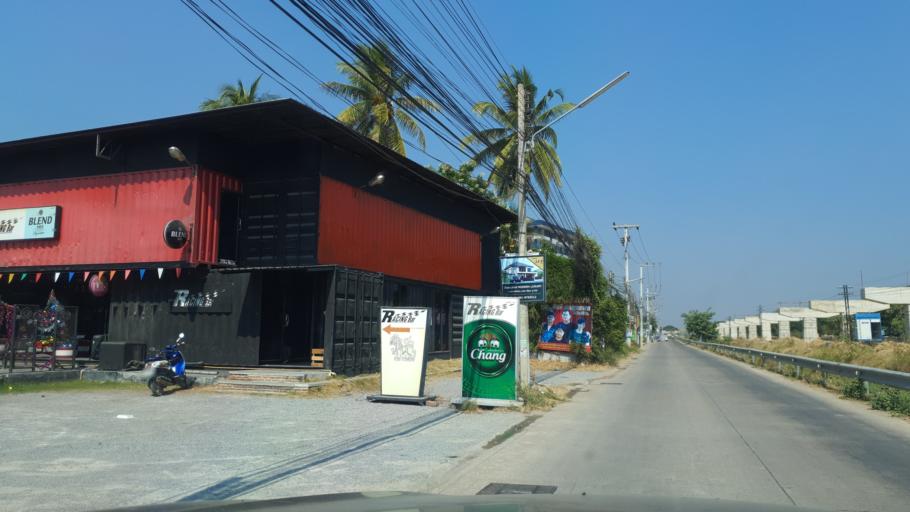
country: TH
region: Prachuap Khiri Khan
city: Hua Hin
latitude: 12.5560
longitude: 99.9572
